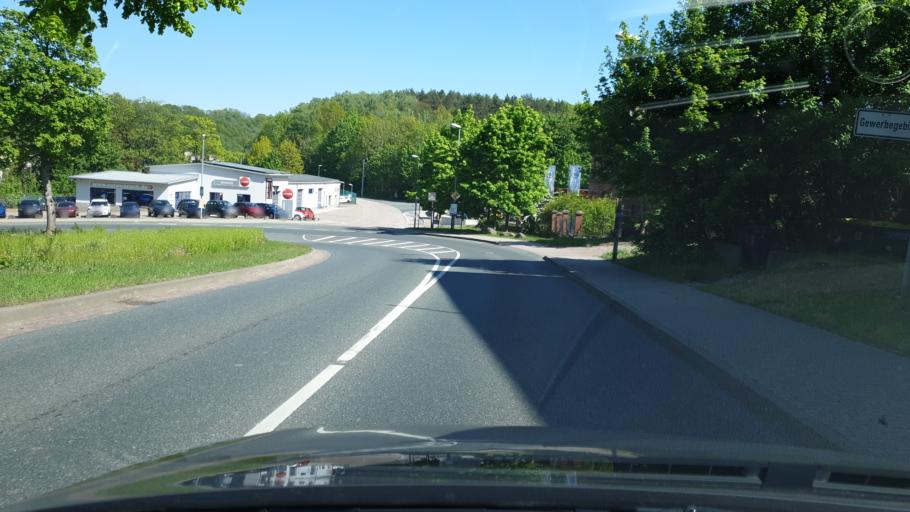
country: DE
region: Saxony
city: Mittweida
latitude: 50.9821
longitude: 12.9917
